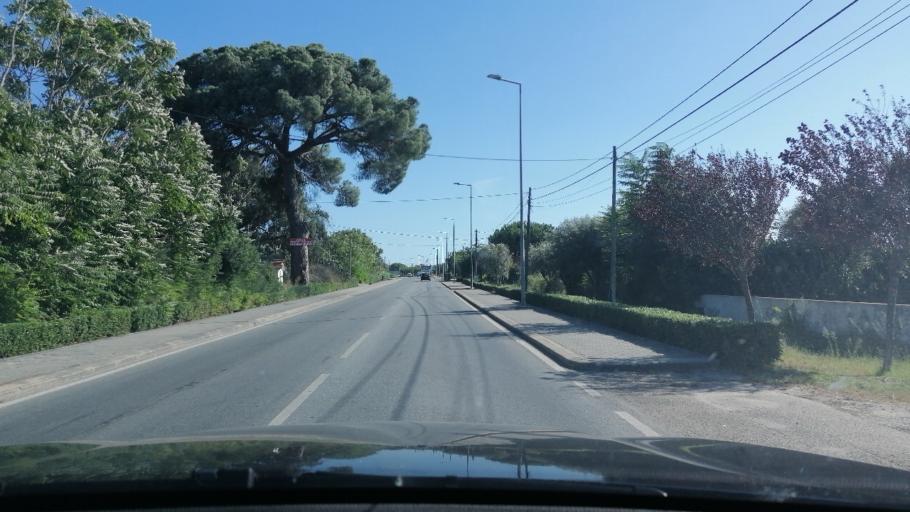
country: PT
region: Setubal
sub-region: Alcacer do Sal
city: Alcacer do Sal
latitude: 38.3837
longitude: -8.5132
